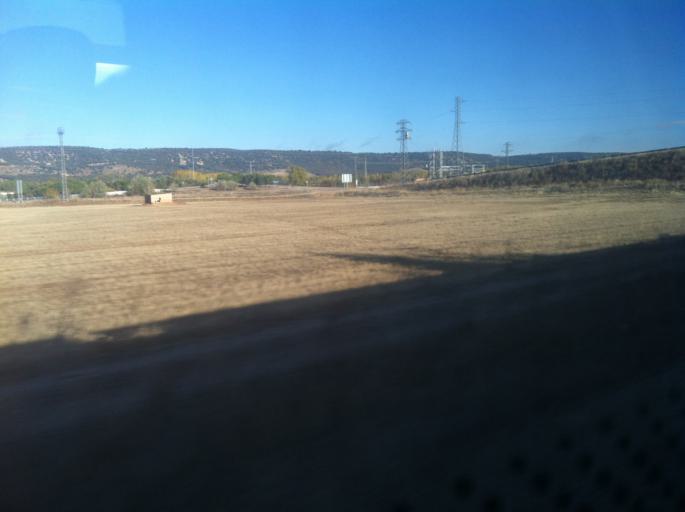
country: ES
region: Castille and Leon
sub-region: Provincia de Palencia
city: Quintana del Puente
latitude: 42.0651
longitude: -4.2219
